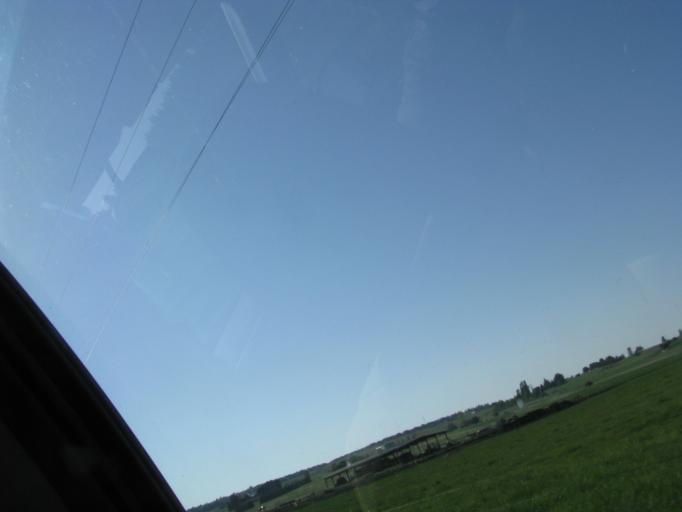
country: US
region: Washington
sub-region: Spokane County
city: Liberty Lake
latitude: 47.6278
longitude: -117.1437
